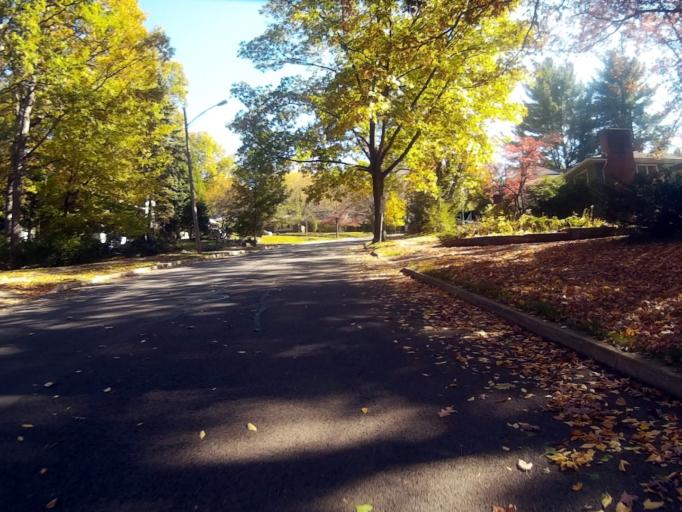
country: US
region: Pennsylvania
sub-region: Centre County
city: State College
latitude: 40.7992
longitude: -77.8776
